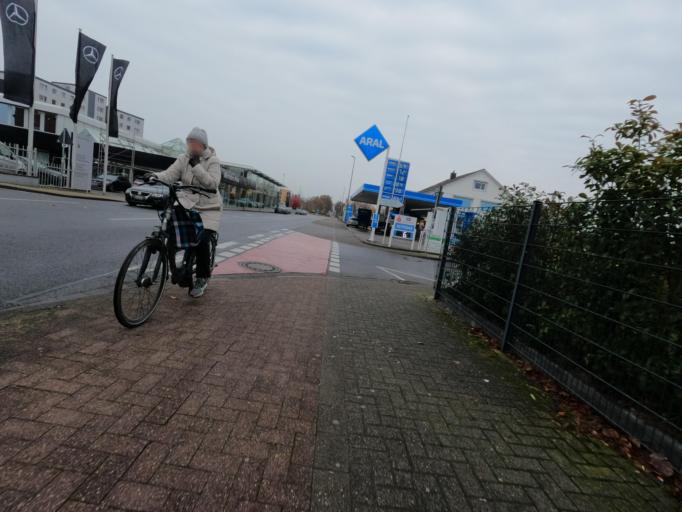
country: DE
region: North Rhine-Westphalia
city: Geilenkirchen
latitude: 50.9702
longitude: 6.1195
